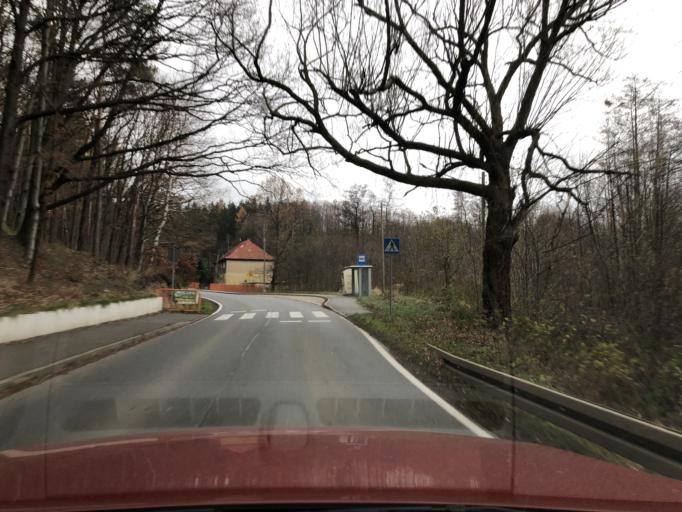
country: PL
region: Lower Silesian Voivodeship
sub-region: Powiat walbrzyski
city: Szczawno-Zdroj
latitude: 50.8107
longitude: 16.2241
